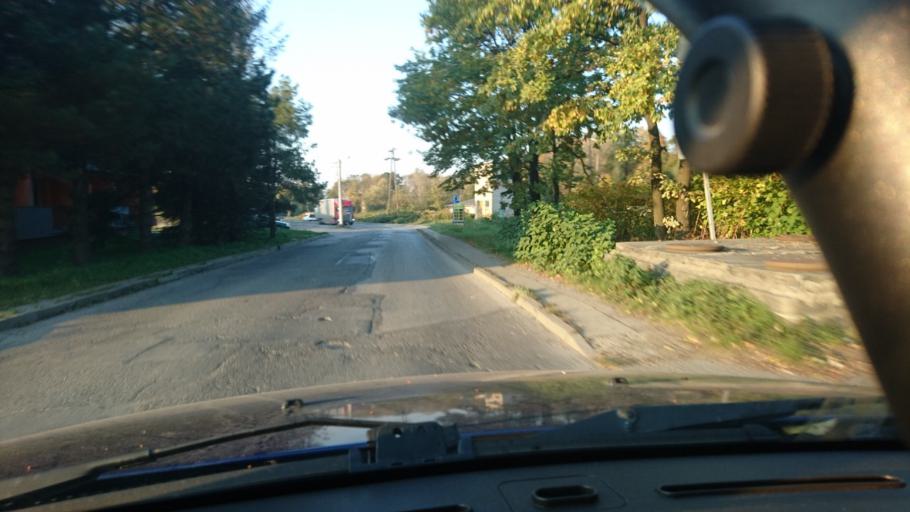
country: PL
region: Silesian Voivodeship
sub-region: Powiat bielski
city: Jaworze
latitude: 49.8150
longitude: 18.9827
